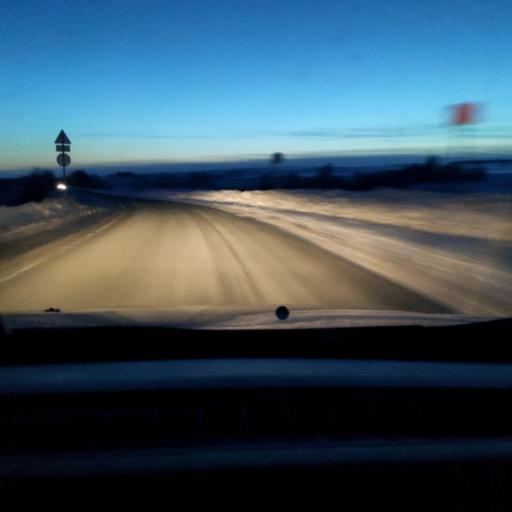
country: RU
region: Samara
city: Kinel'
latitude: 53.2953
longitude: 50.6909
